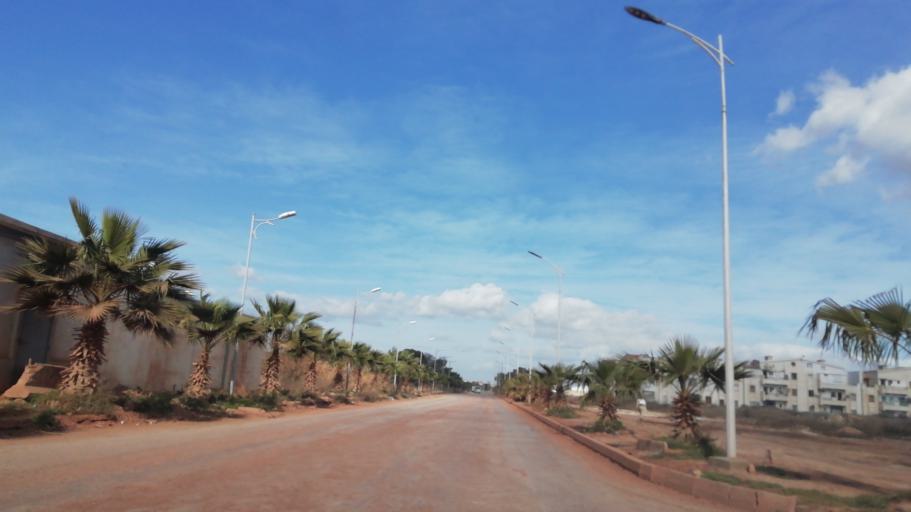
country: DZ
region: Oran
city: Es Senia
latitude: 35.6296
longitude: -0.5843
